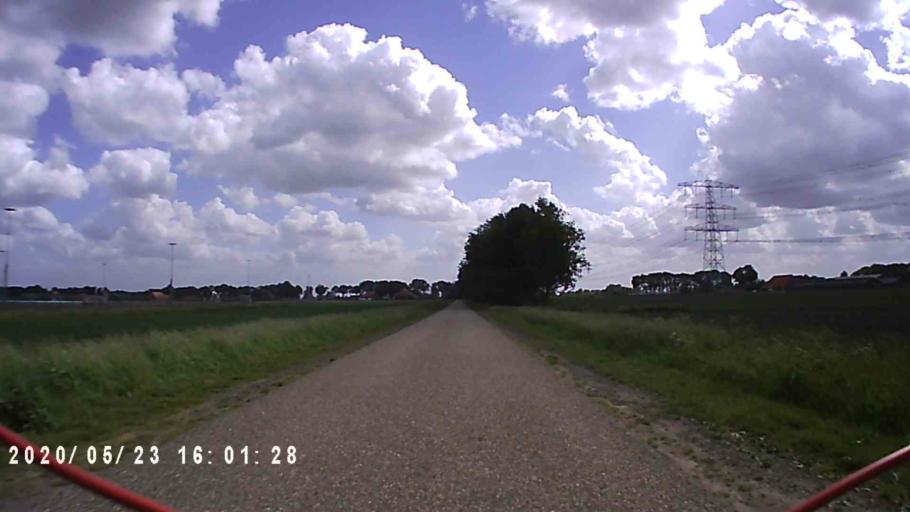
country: NL
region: Groningen
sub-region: Gemeente Delfzijl
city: Delfzijl
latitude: 53.2491
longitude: 6.9000
